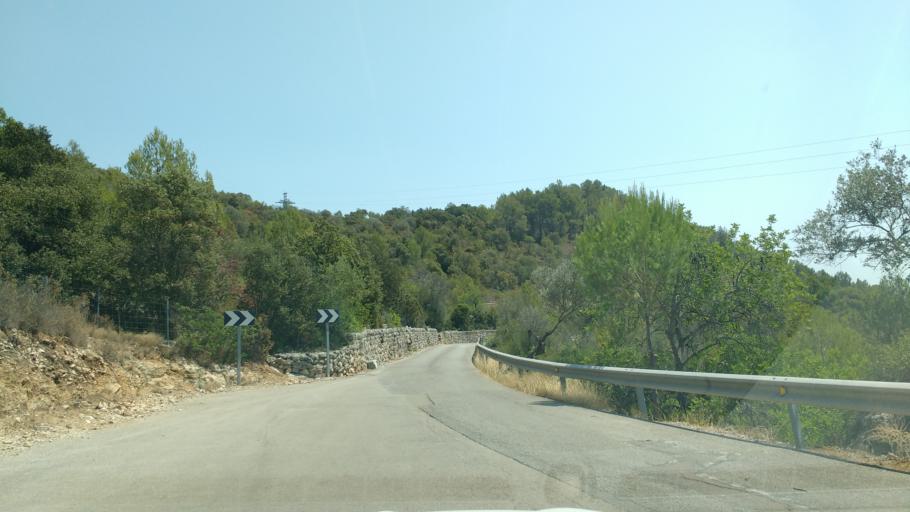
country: ES
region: Balearic Islands
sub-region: Illes Balears
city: Lloseta
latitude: 39.7228
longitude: 2.8353
